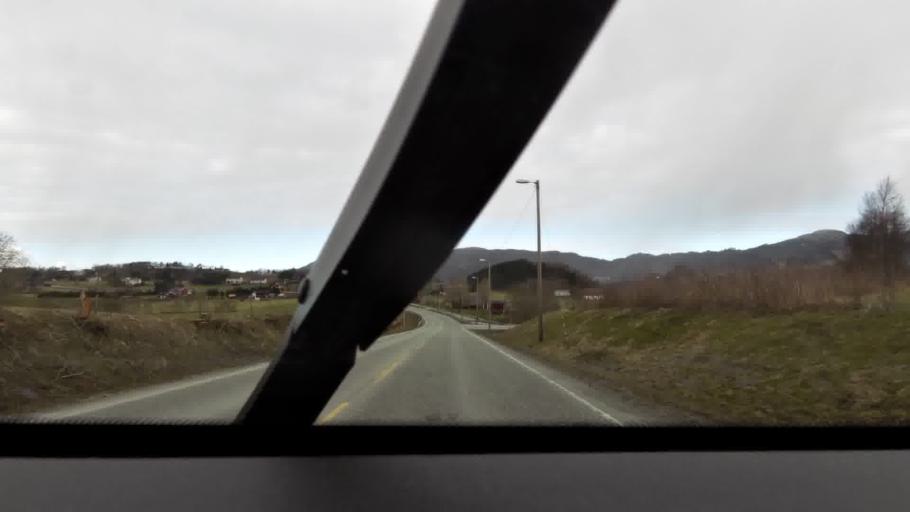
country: NO
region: More og Romsdal
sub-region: Eide
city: Eide
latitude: 62.9486
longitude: 7.4147
